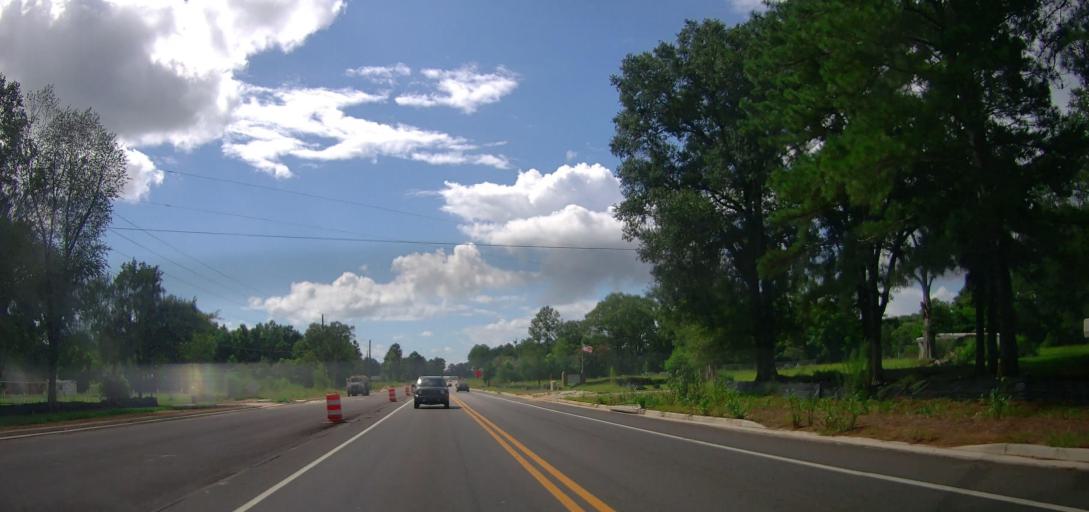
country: US
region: Georgia
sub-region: Coffee County
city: Douglas
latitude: 31.5260
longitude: -82.9030
